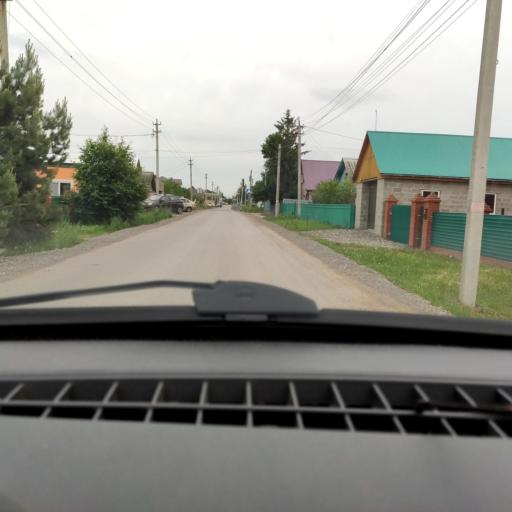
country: RU
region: Bashkortostan
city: Ufa
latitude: 54.6430
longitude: 55.9207
